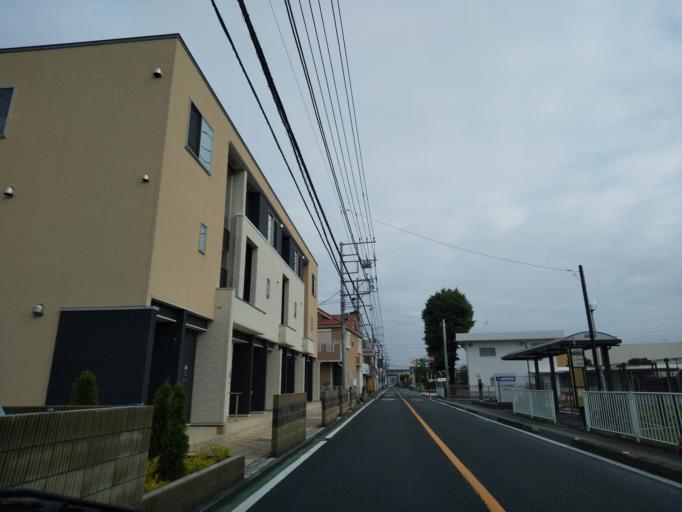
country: JP
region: Tokyo
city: Hino
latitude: 35.6713
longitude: 139.4034
